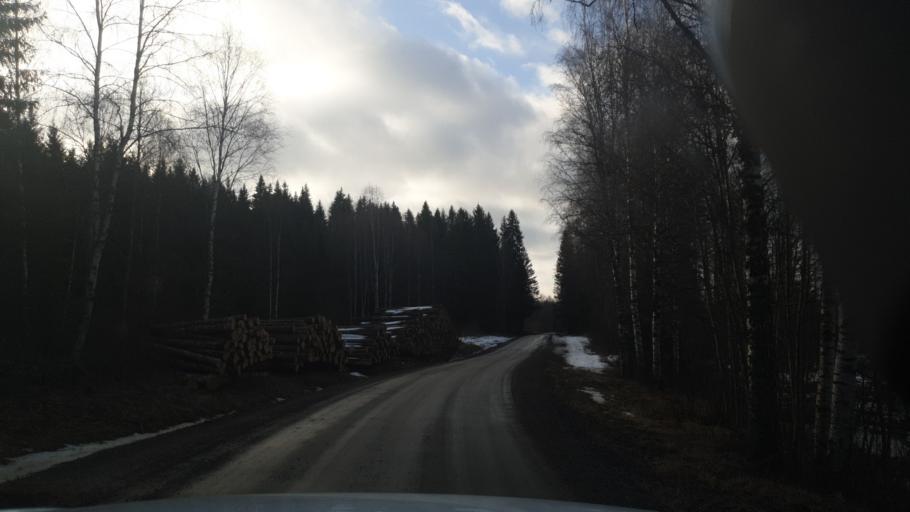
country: SE
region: Vaermland
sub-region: Eda Kommun
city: Amotfors
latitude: 59.7790
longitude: 12.4378
